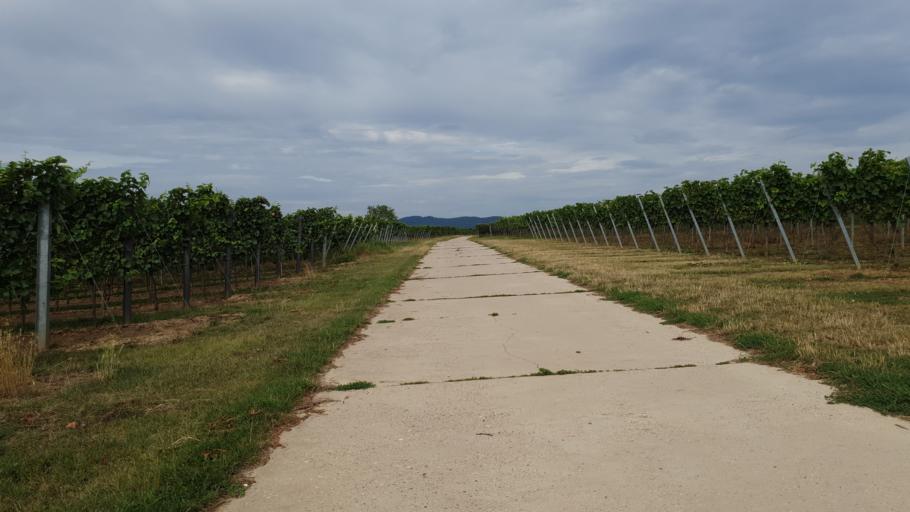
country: DE
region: Rheinland-Pfalz
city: Billigheim-Ingenheim
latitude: 49.1277
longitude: 8.0781
